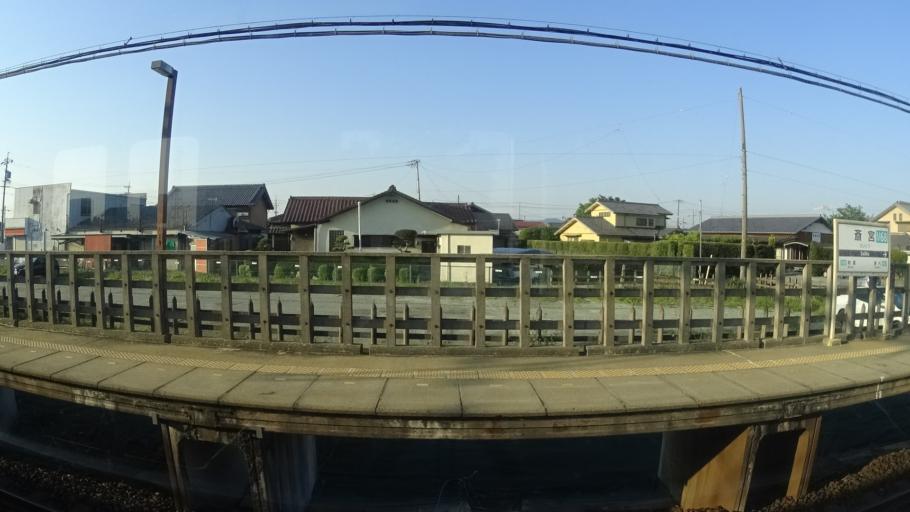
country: JP
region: Mie
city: Ise
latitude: 34.5379
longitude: 136.6147
